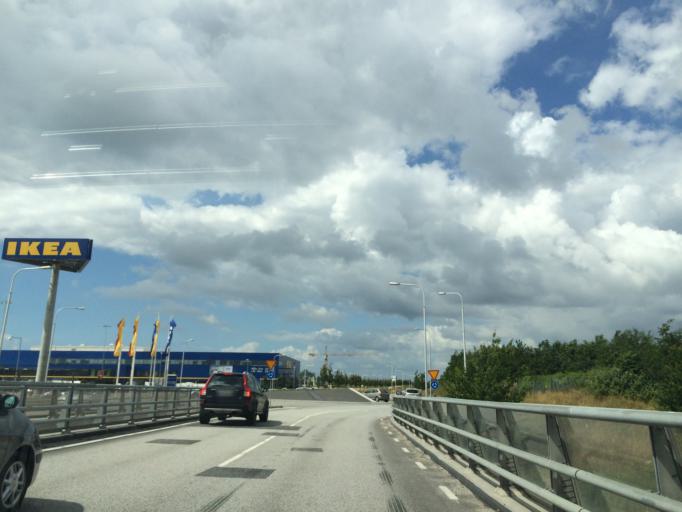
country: SE
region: Skane
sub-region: Malmo
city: Tygelsjo
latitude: 55.5541
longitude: 12.9913
